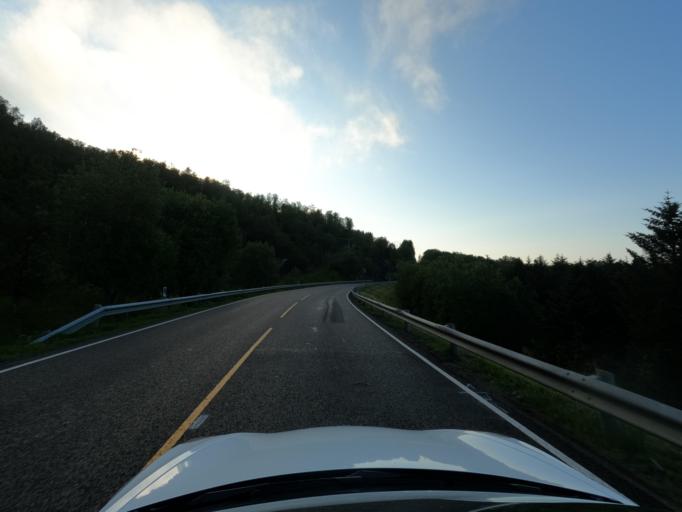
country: NO
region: Troms
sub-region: Skanland
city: Evenskjer
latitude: 68.6713
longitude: 16.5715
